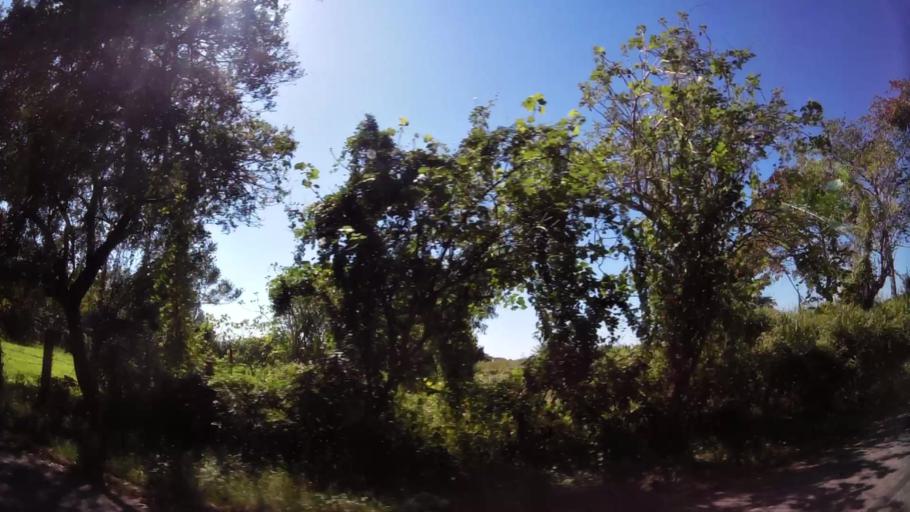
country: GT
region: Escuintla
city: Iztapa
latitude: 13.9194
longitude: -90.5614
